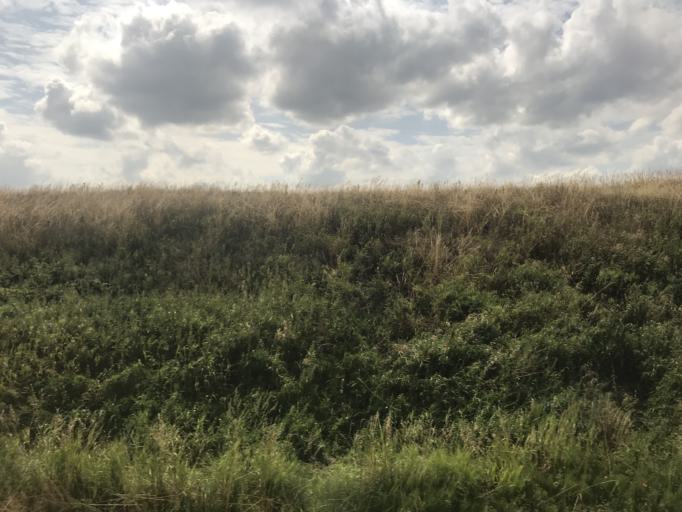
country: PL
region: Greater Poland Voivodeship
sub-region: Powiat gnieznienski
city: Lubowo
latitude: 52.4937
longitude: 17.3848
